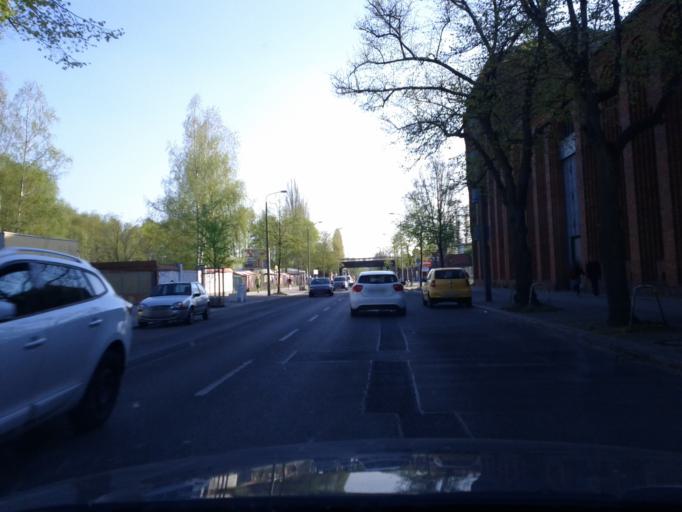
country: DE
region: Berlin
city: Wilhelmsruh
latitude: 52.5825
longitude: 13.3645
